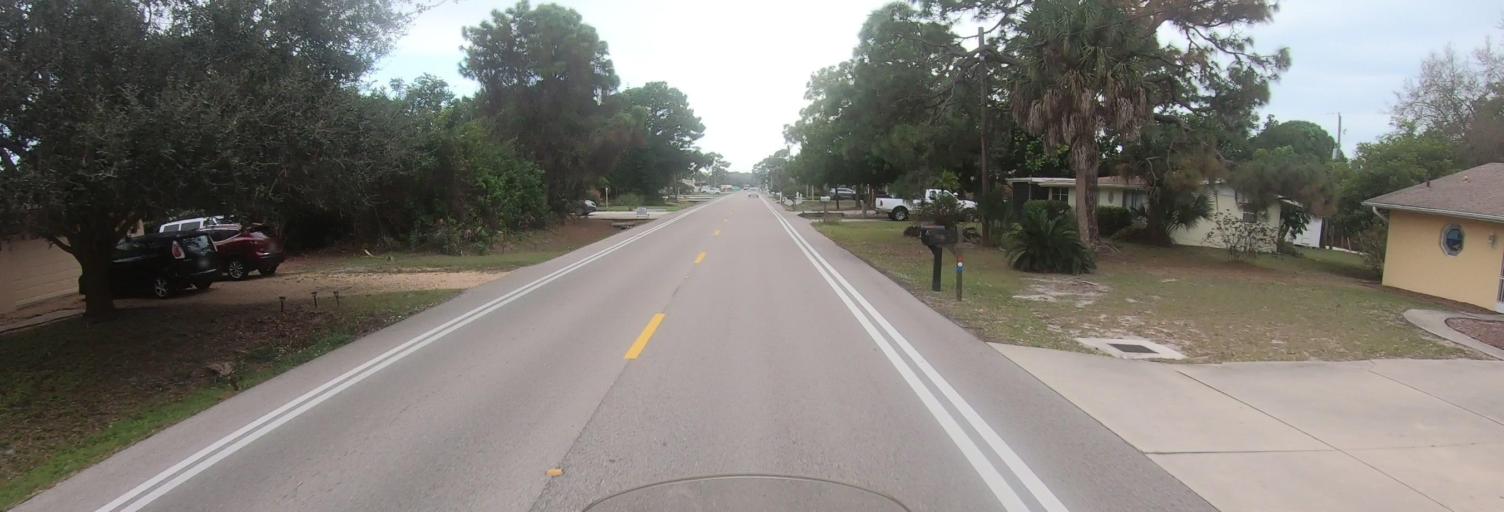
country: US
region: Florida
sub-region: Sarasota County
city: South Venice
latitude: 27.0648
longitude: -82.4291
